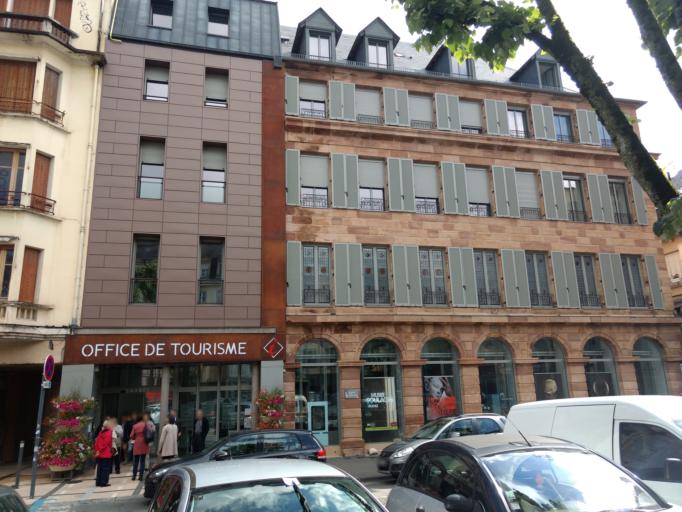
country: FR
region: Midi-Pyrenees
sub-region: Departement de l'Aveyron
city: Rodez
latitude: 44.3510
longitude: 2.5760
